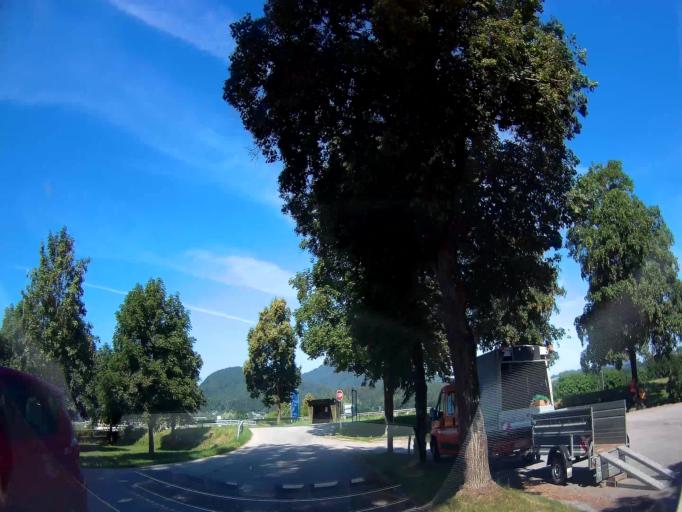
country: AT
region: Carinthia
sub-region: Politischer Bezirk Klagenfurt Land
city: Maria Saal
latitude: 46.6904
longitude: 14.3461
